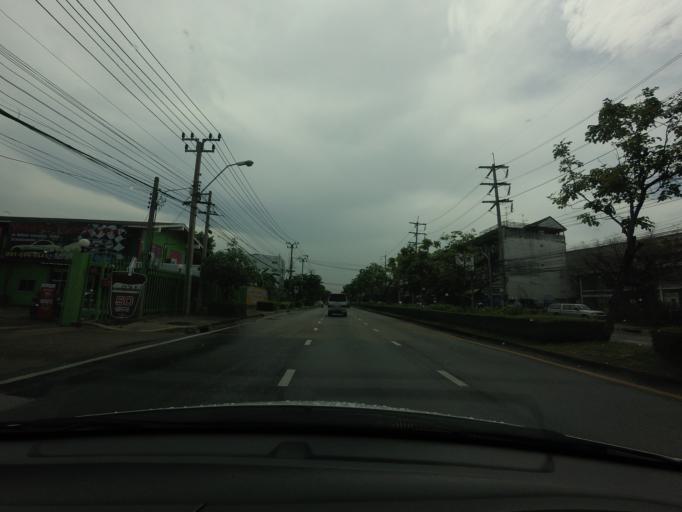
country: TH
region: Bangkok
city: Suan Luang
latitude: 13.7170
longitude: 100.6581
